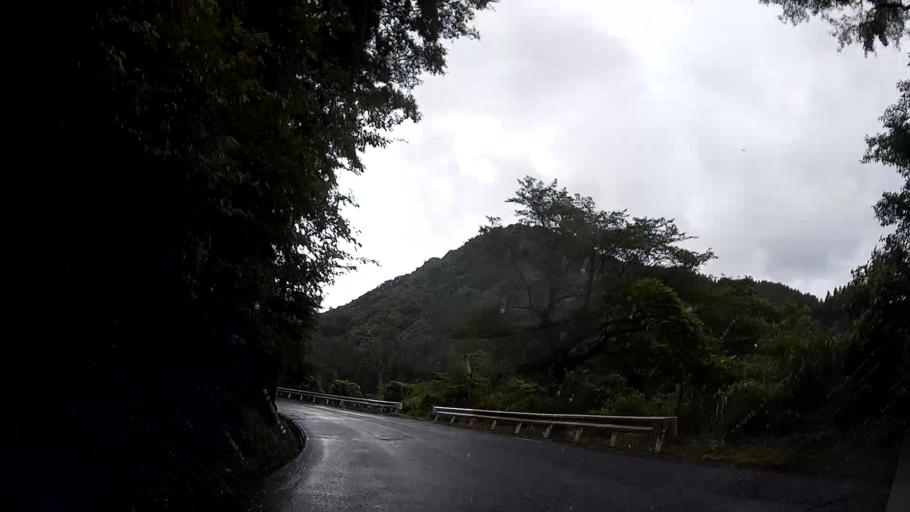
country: JP
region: Oita
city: Hita
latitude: 33.1828
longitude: 130.9984
